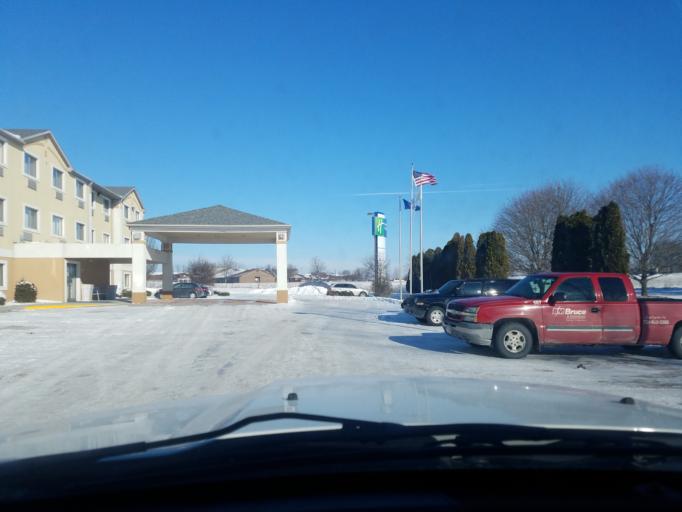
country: US
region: Indiana
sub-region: Noble County
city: Kendallville
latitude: 41.4455
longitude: -85.2331
